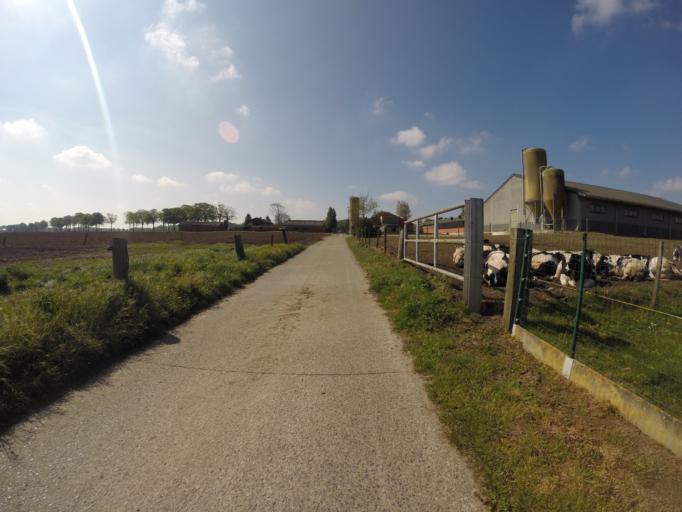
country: BE
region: Flanders
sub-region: Provincie West-Vlaanderen
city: Beernem
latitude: 51.0960
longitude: 3.3427
